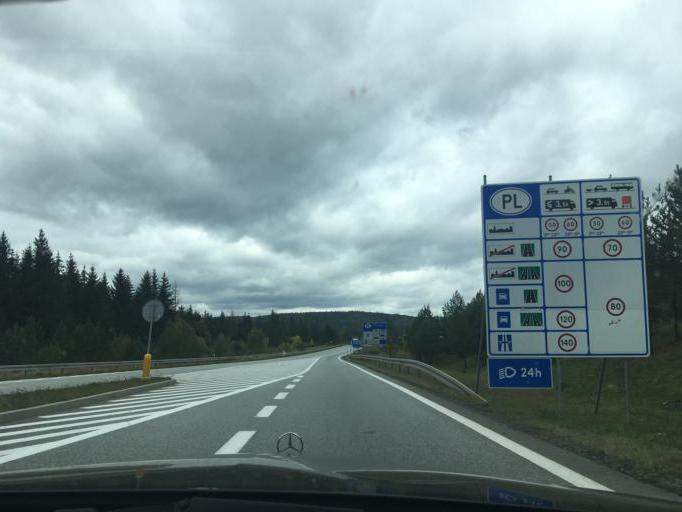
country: PL
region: Subcarpathian Voivodeship
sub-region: Powiat krosnienski
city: Jasliska
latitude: 49.4213
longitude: 21.6941
